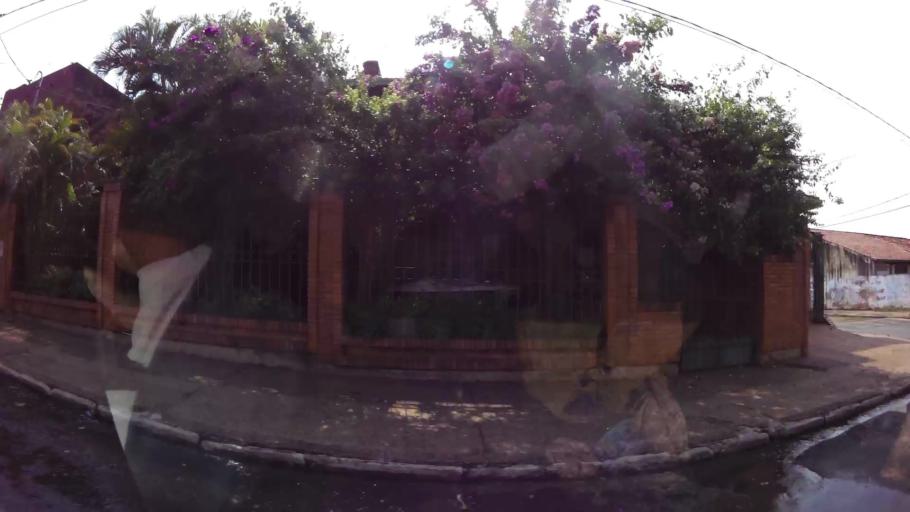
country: PY
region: Presidente Hayes
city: Nanawa
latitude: -25.2919
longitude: -57.6625
